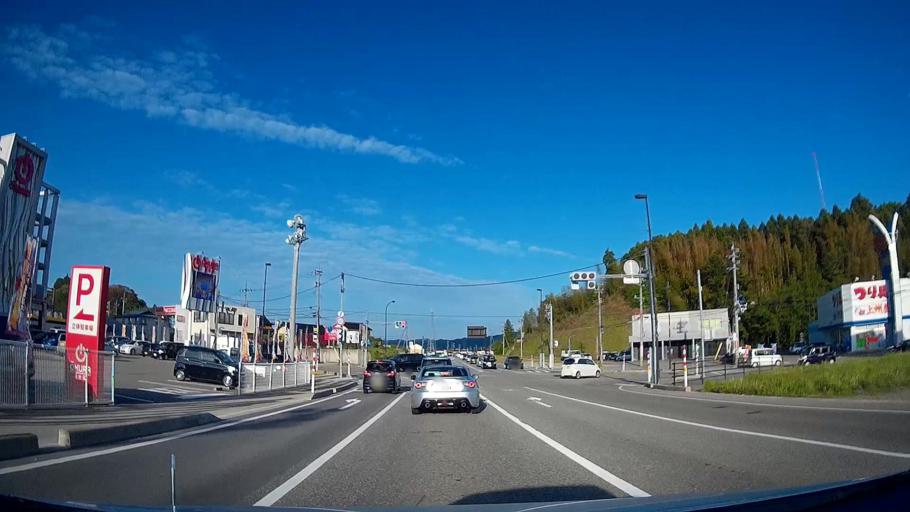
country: JP
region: Ishikawa
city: Nanao
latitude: 37.0343
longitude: 136.9515
